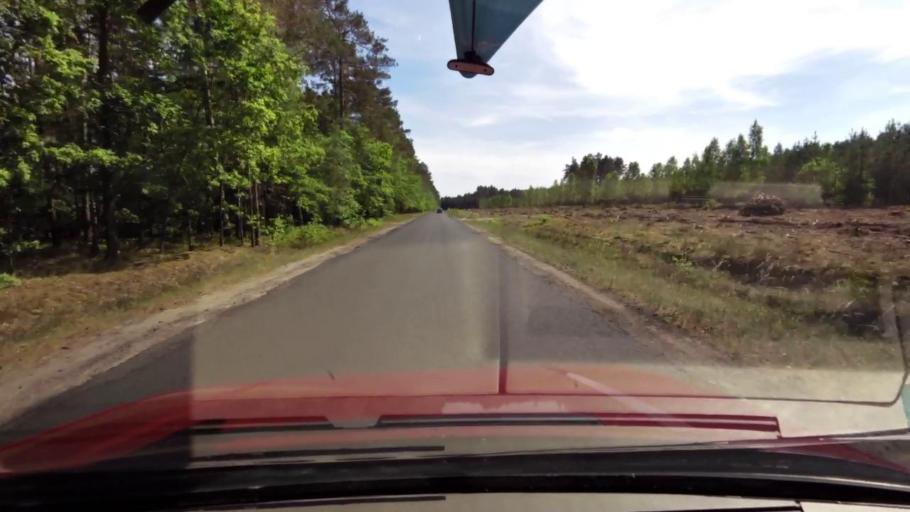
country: PL
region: Pomeranian Voivodeship
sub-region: Powiat slupski
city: Kepice
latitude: 54.2985
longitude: 16.9611
